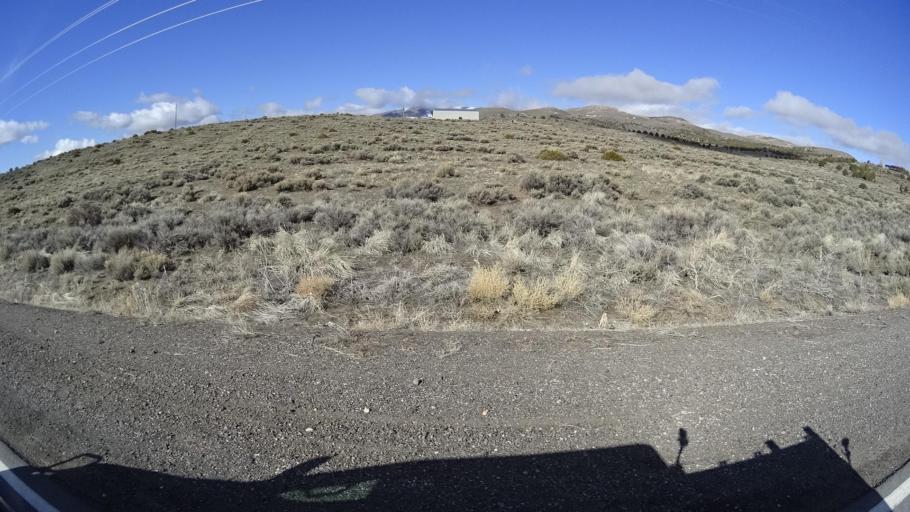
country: US
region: Nevada
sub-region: Washoe County
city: Cold Springs
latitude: 39.7620
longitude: -119.8857
